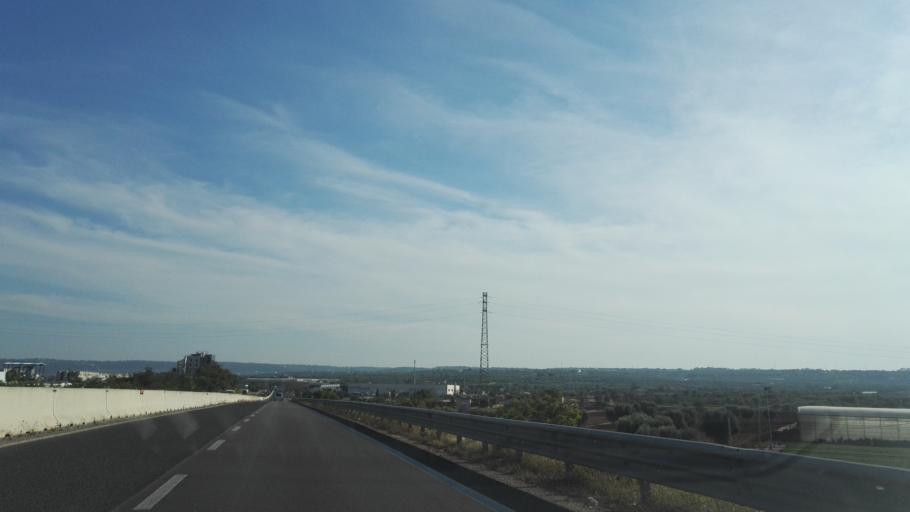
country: IT
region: Apulia
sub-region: Provincia di Bari
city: Monopoli
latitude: 40.9654
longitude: 17.2615
